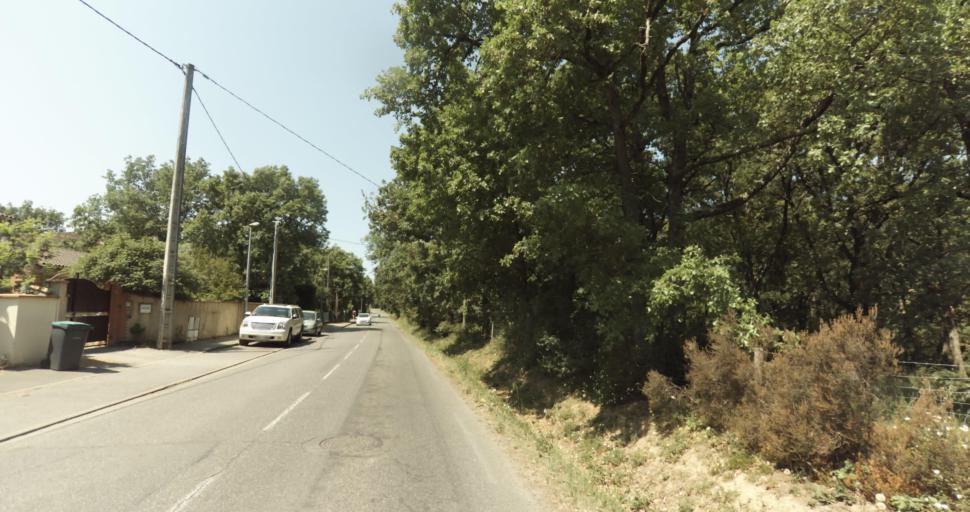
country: FR
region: Midi-Pyrenees
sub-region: Departement de la Haute-Garonne
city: La Salvetat-Saint-Gilles
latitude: 43.5761
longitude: 1.2557
